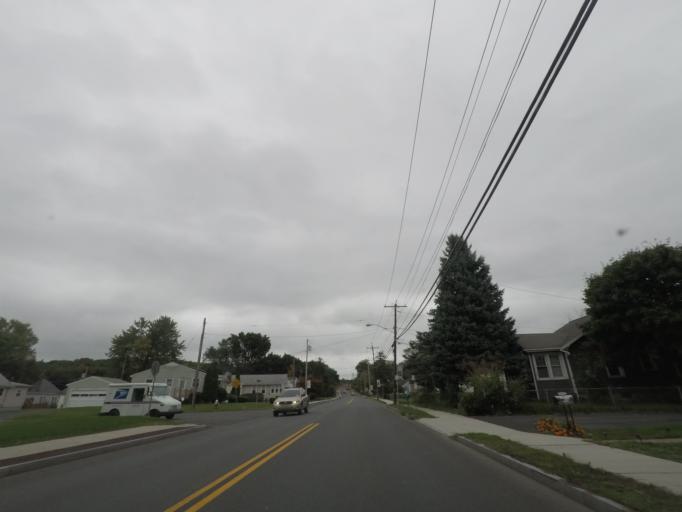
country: US
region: New York
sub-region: Rensselaer County
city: Rensselaer
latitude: 42.6549
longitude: -73.7064
